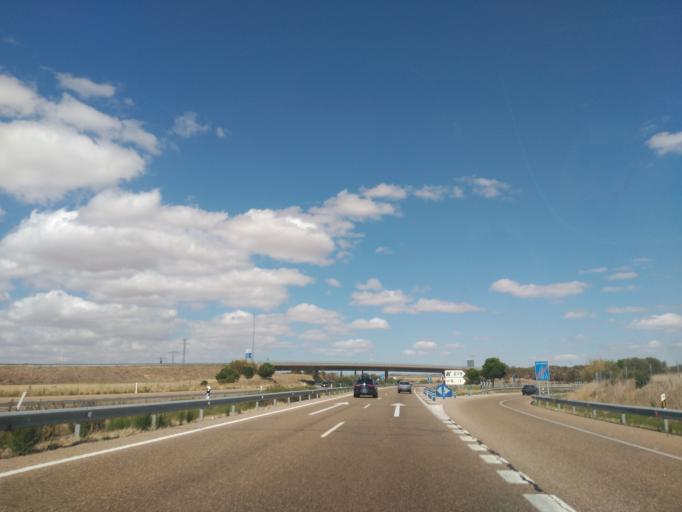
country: ES
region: Castille and Leon
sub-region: Provincia de Salamanca
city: Pajares de la Laguna
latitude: 41.0905
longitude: -5.5030
